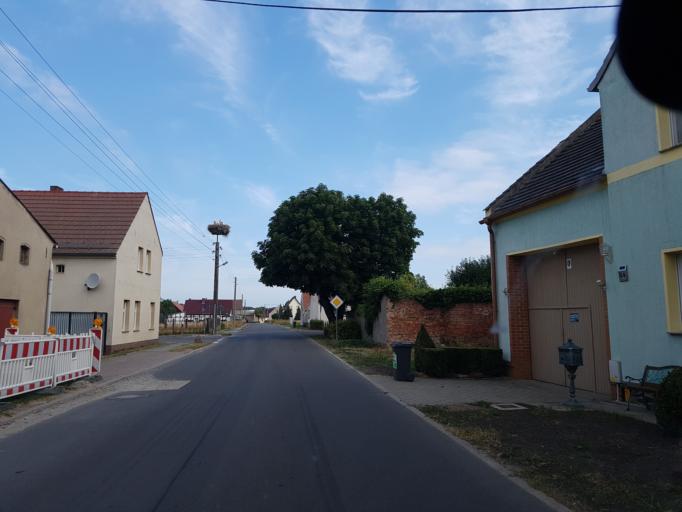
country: DE
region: Brandenburg
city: Luckau
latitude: 51.8397
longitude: 13.6385
